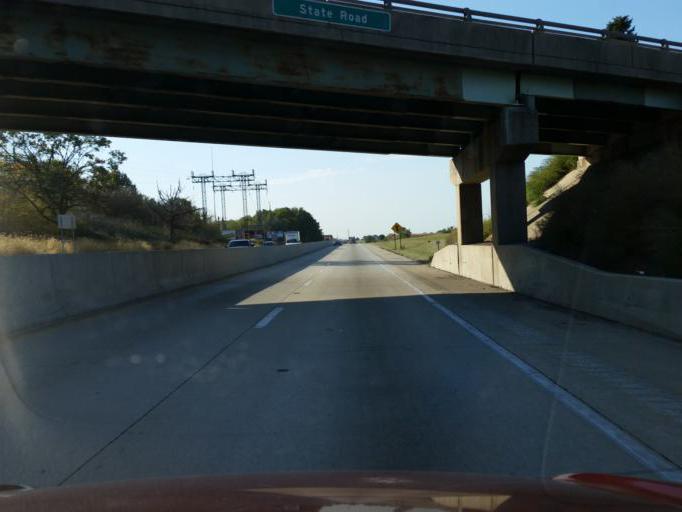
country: US
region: Pennsylvania
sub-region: Lancaster County
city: East Petersburg
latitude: 40.0888
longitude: -76.3804
